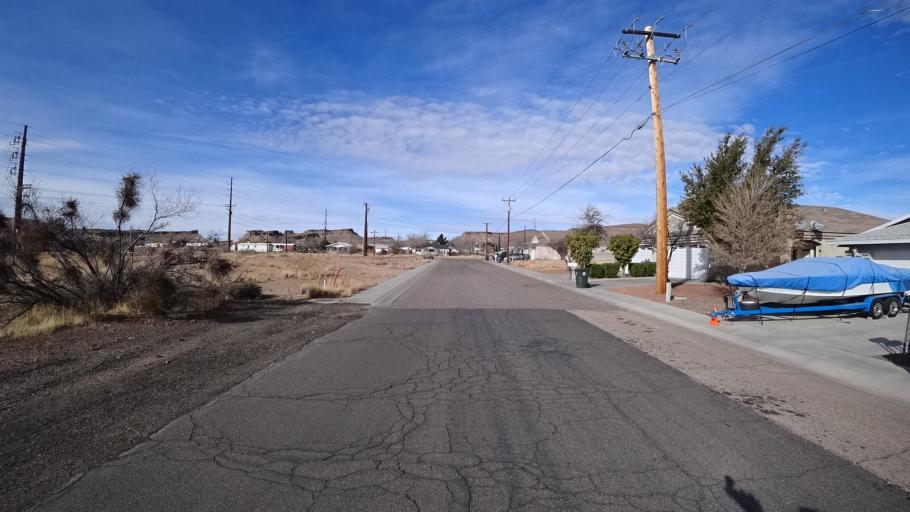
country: US
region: Arizona
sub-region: Mohave County
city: Kingman
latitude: 35.2177
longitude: -114.0436
